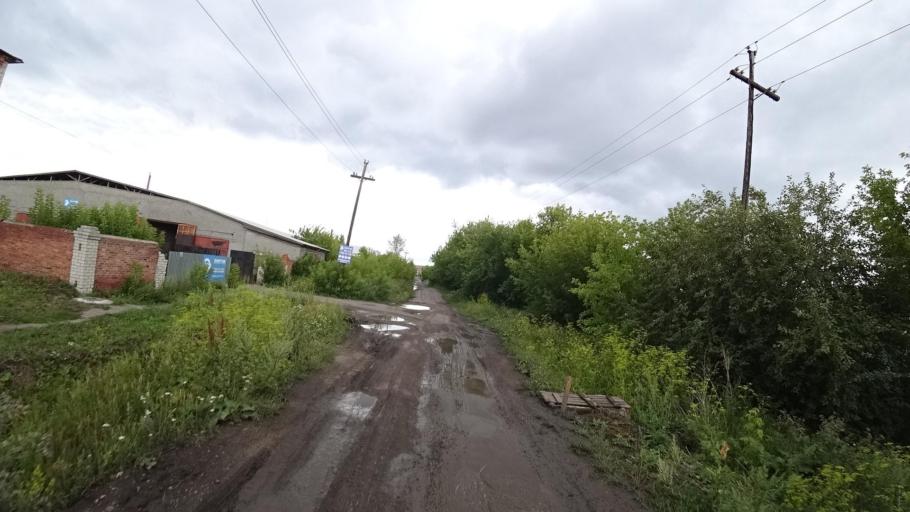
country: RU
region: Sverdlovsk
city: Kamyshlov
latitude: 56.8489
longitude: 62.7355
